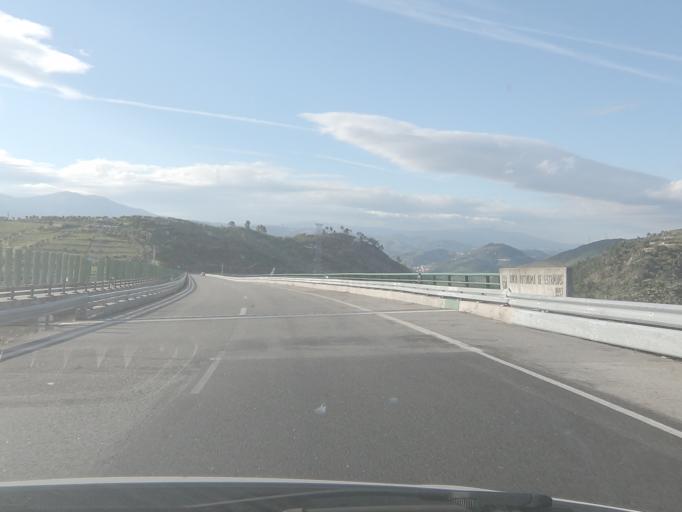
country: PT
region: Viseu
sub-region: Lamego
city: Lamego
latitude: 41.1102
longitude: -7.7762
